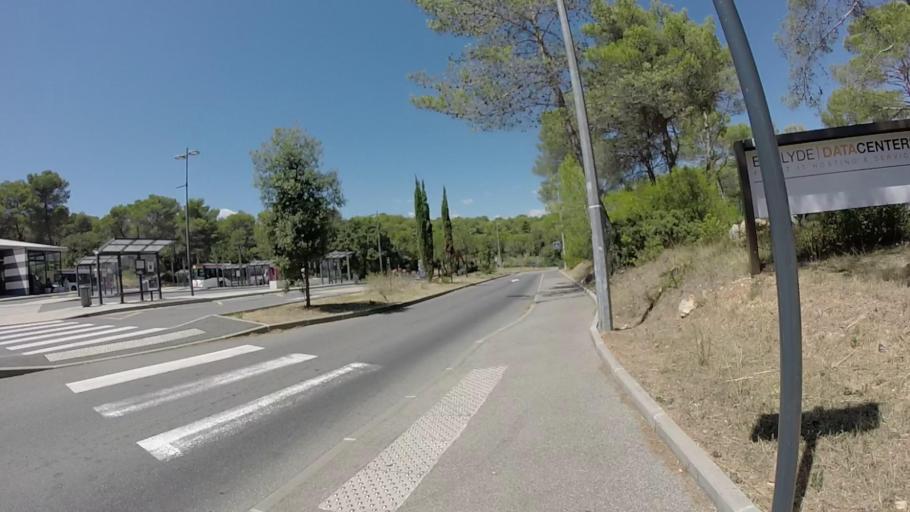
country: FR
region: Provence-Alpes-Cote d'Azur
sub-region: Departement des Alpes-Maritimes
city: Valbonne
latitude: 43.6238
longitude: 7.0378
